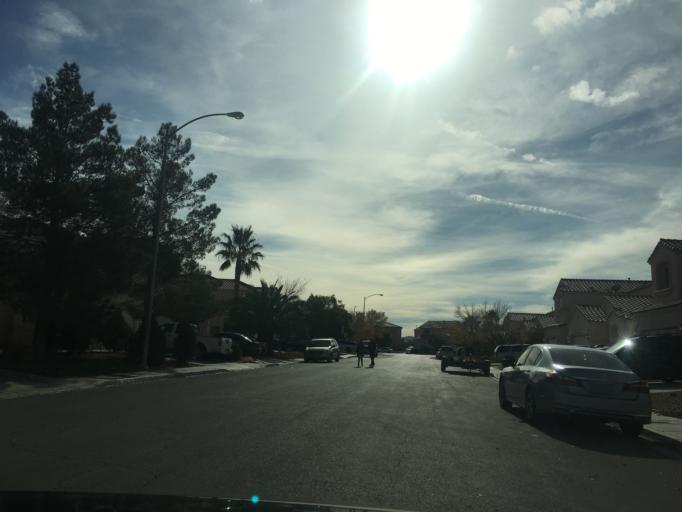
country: US
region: Nevada
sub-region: Clark County
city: Enterprise
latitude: 36.0155
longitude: -115.1684
